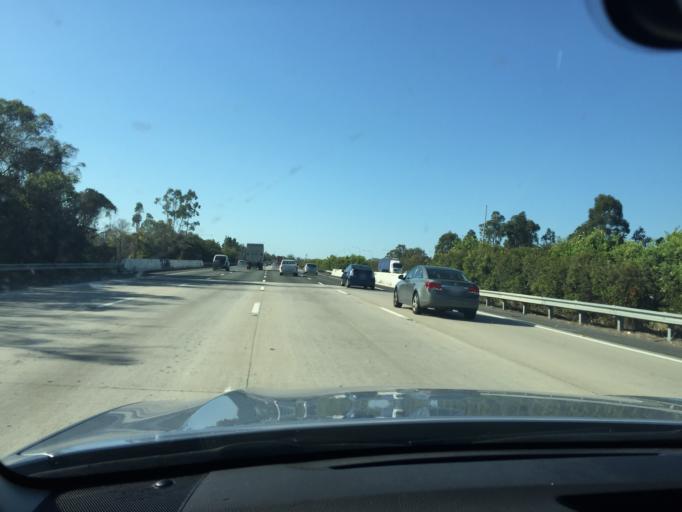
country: AU
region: Queensland
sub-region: Gold Coast
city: Yatala
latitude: -27.7348
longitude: 153.2278
